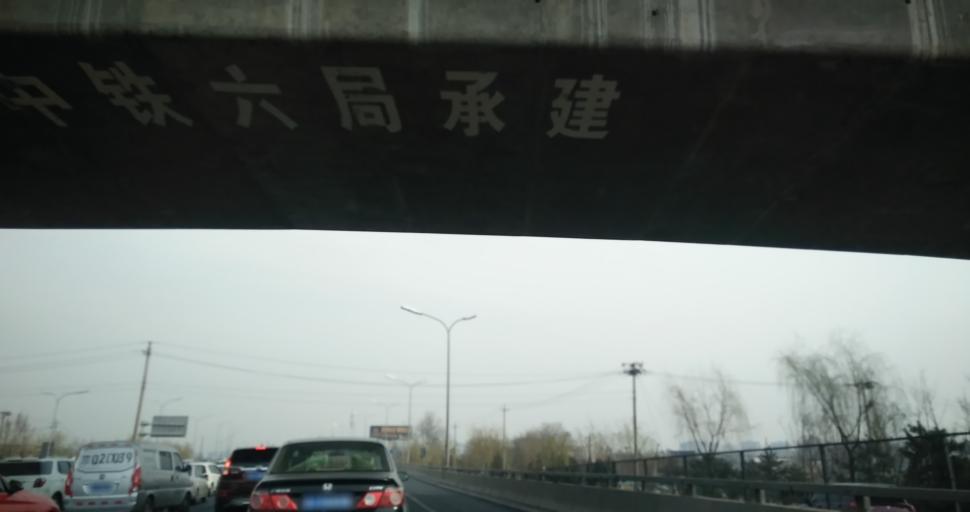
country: CN
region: Beijing
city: Jiugong
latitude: 39.8440
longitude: 116.4767
